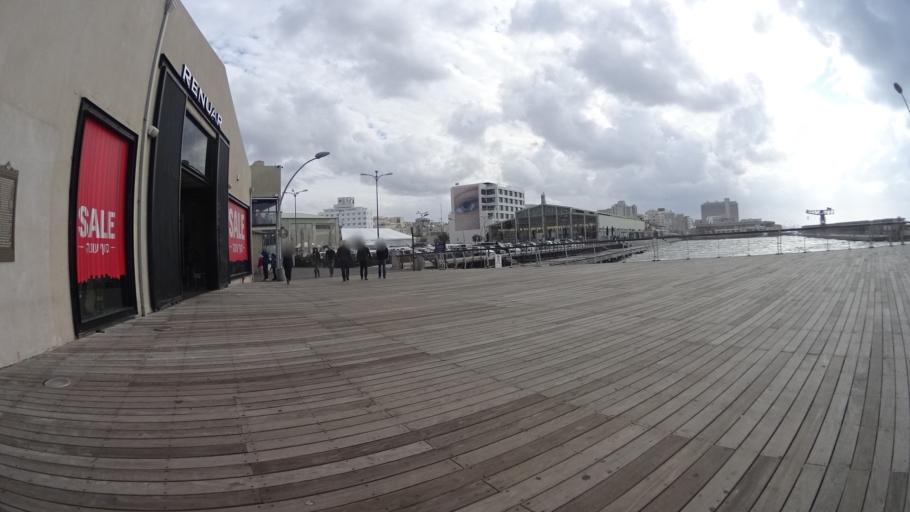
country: IL
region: Tel Aviv
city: Tel Aviv
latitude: 32.0991
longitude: 34.7736
